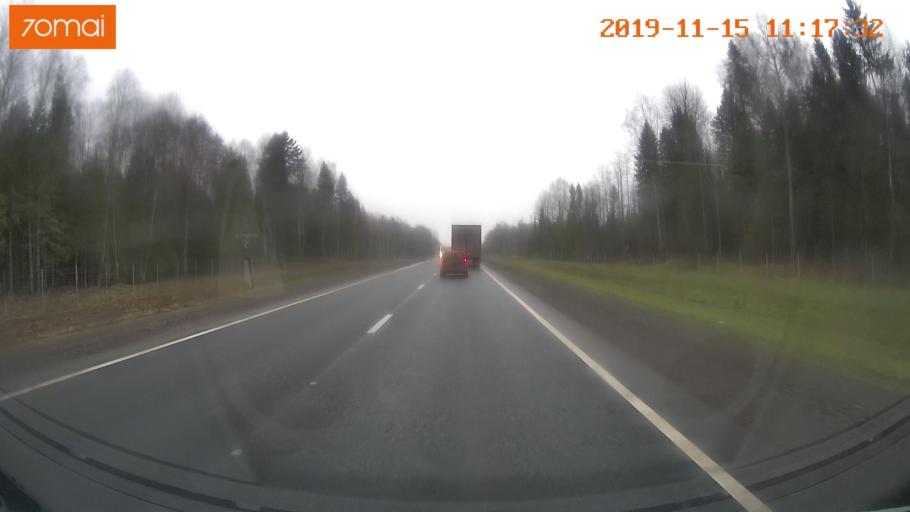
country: RU
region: Vologda
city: Chebsara
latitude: 59.1333
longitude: 39.2530
